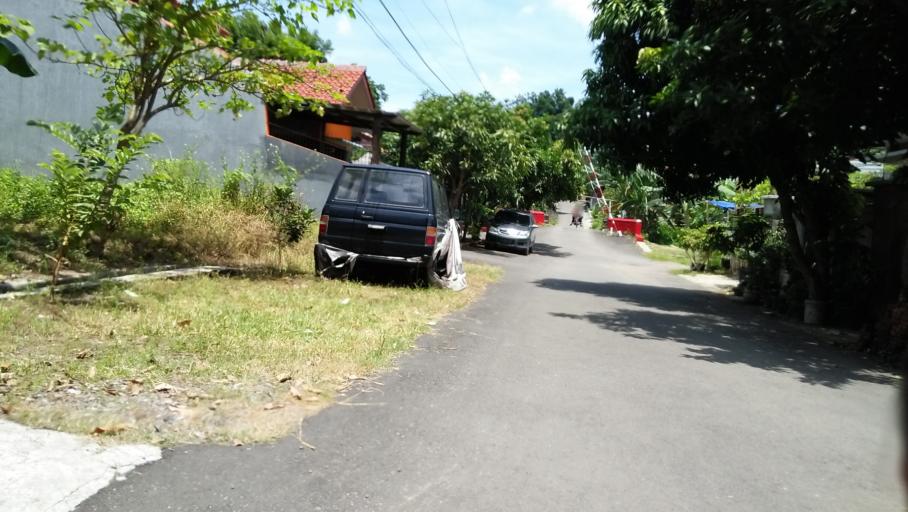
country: ID
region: Central Java
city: Mranggen
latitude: -7.0326
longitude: 110.4608
